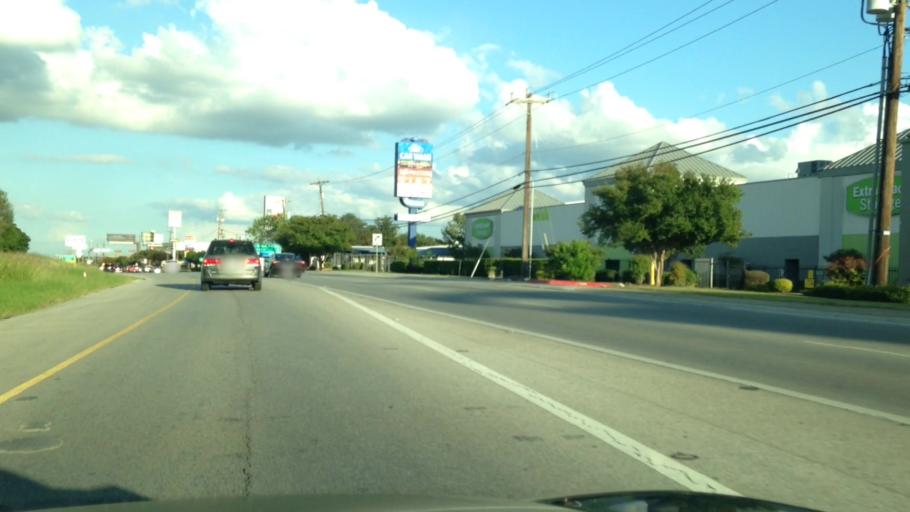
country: US
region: Texas
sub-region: Bexar County
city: Hollywood Park
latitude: 29.6081
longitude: -98.4953
